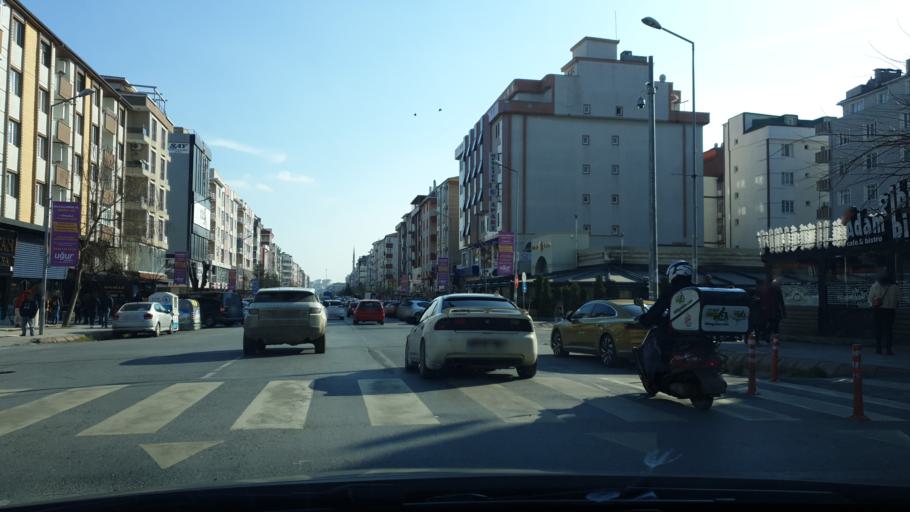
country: TR
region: Tekirdag
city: Cerkezkoey
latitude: 41.2929
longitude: 27.9980
